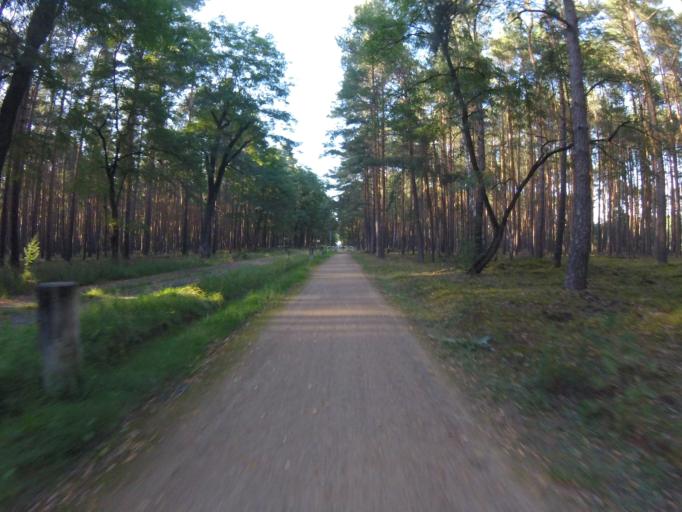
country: DE
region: Brandenburg
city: Munchehofe
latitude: 52.2119
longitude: 13.7718
